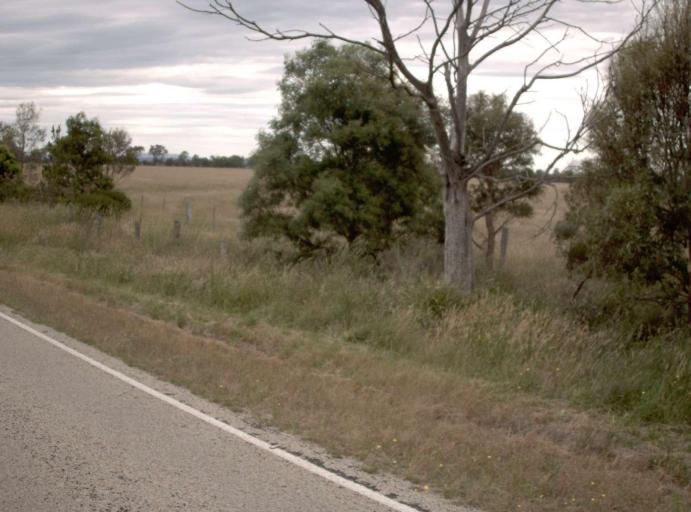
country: AU
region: Victoria
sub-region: East Gippsland
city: Bairnsdale
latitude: -37.9052
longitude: 147.5517
